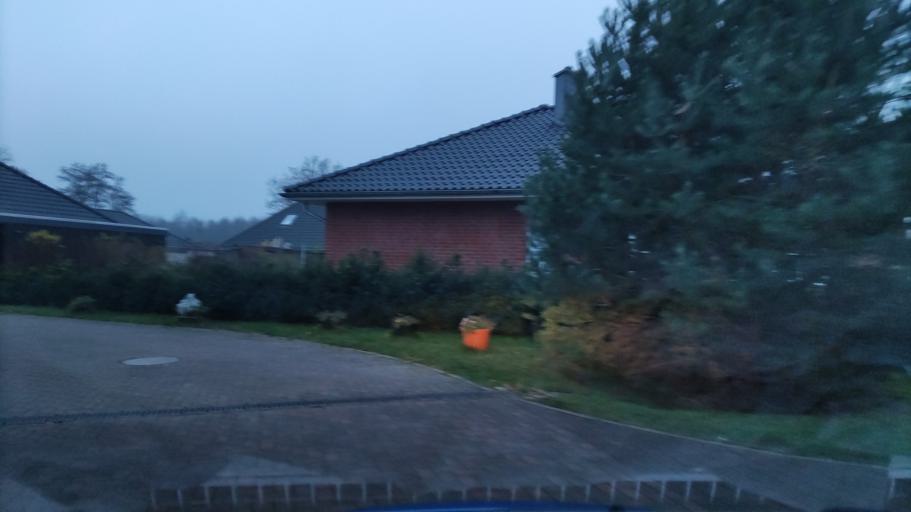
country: DE
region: Lower Saxony
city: Dahlenburg
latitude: 53.1792
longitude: 10.7566
